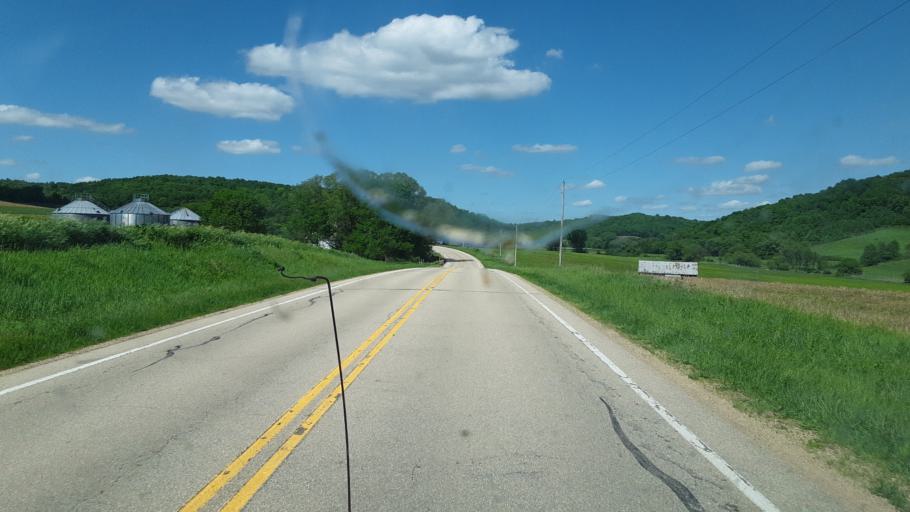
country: US
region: Wisconsin
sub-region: Richland County
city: Richland Center
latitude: 43.4488
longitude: -90.2285
